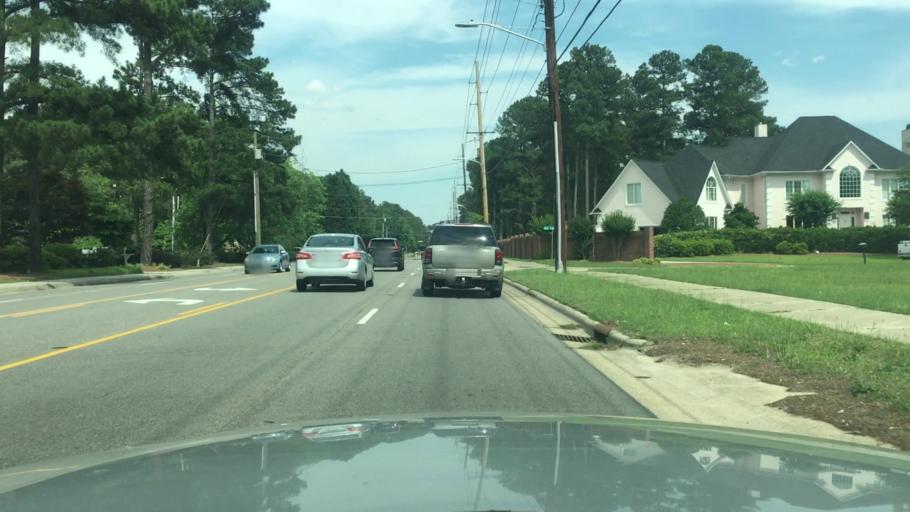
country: US
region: North Carolina
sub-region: Cumberland County
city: Fayetteville
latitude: 35.0658
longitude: -78.9442
